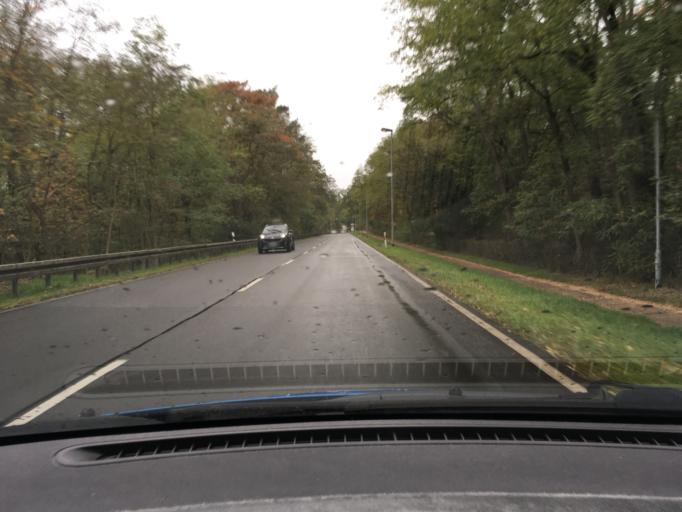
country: DE
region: Saxony-Anhalt
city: Rosslau
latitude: 51.8891
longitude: 12.2672
